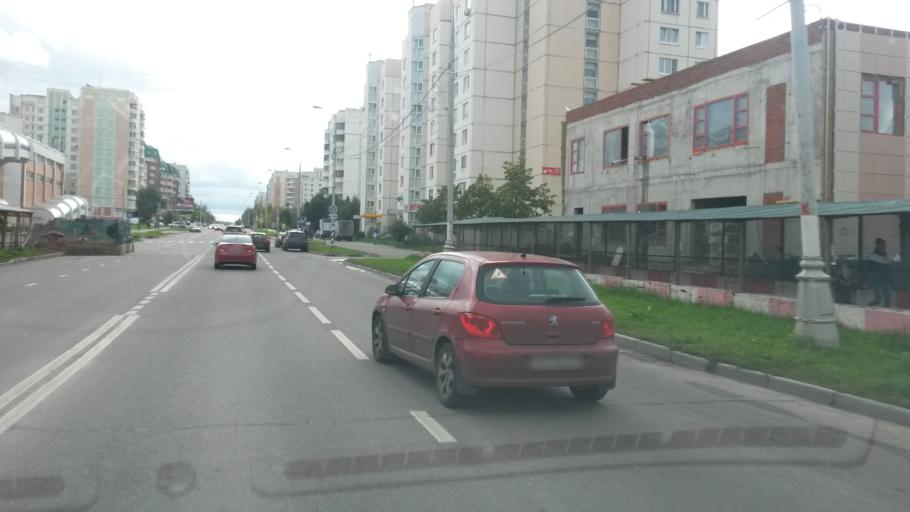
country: RU
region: Moskovskaya
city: Kommunarka
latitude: 55.5363
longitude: 37.5149
